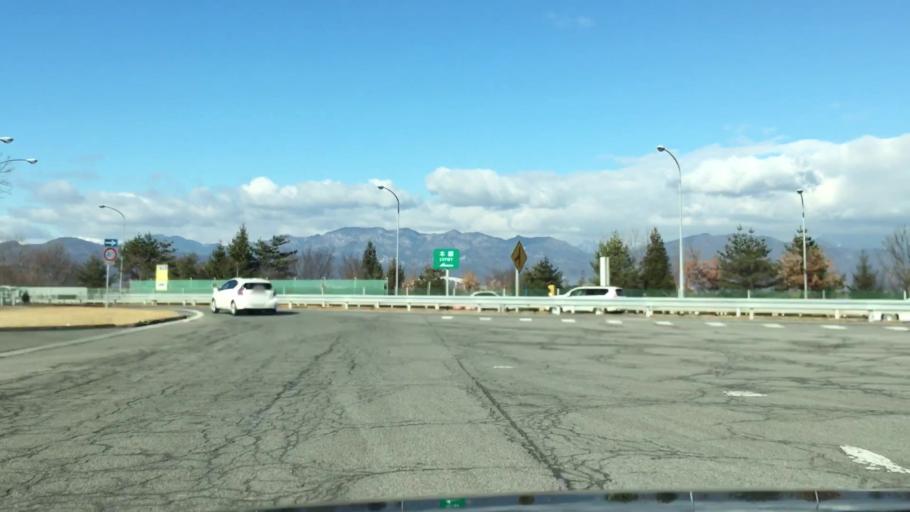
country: JP
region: Nagano
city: Nagano-shi
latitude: 36.5634
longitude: 138.1815
